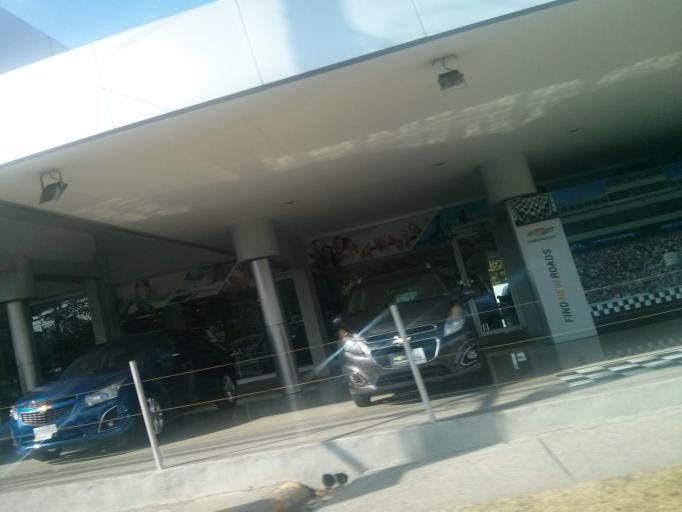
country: CR
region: San Jose
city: Colima
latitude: 9.9490
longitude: -84.0980
